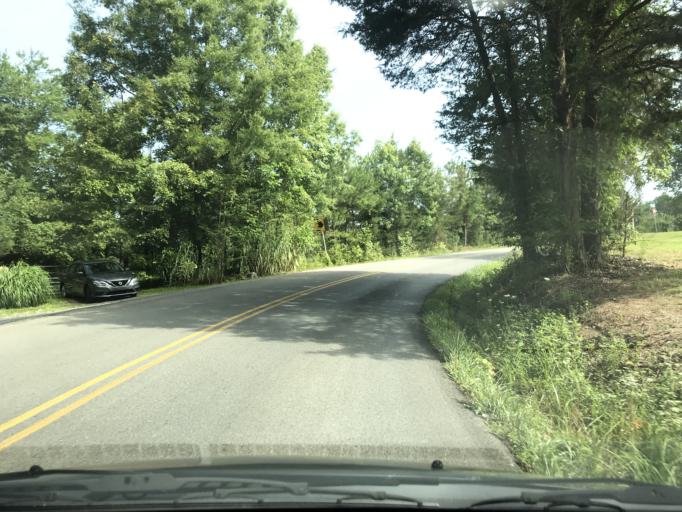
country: US
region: Tennessee
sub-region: Hamilton County
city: Apison
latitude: 35.0705
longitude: -84.9784
